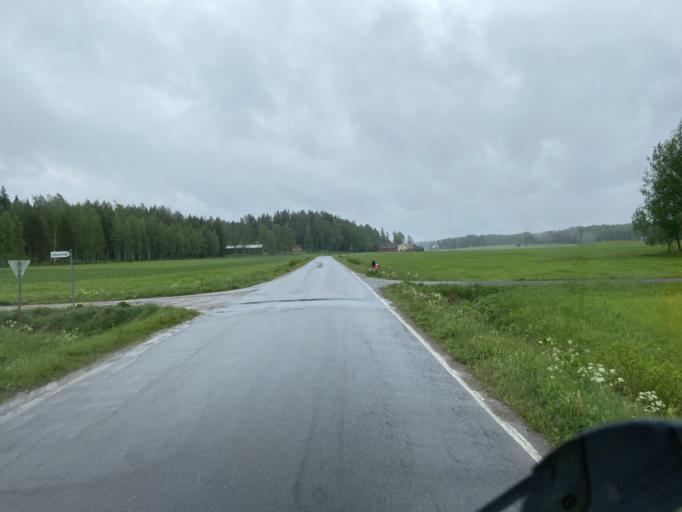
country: FI
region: Haeme
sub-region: Forssa
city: Humppila
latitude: 61.0499
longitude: 23.3623
